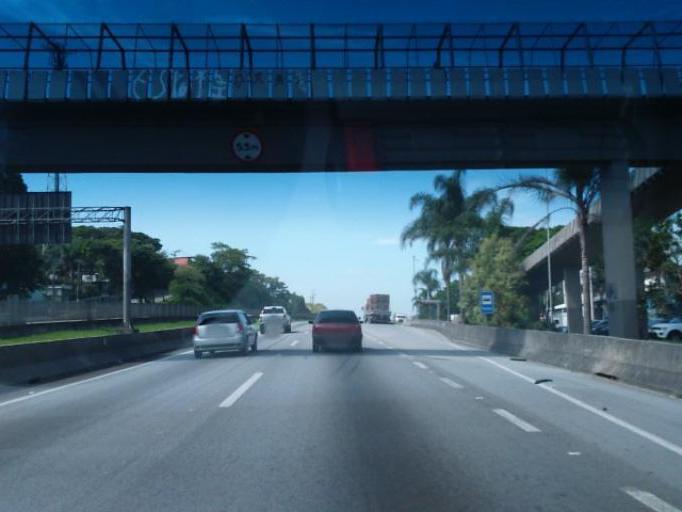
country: BR
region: Sao Paulo
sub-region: Embu
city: Embu
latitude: -23.6537
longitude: -46.8487
